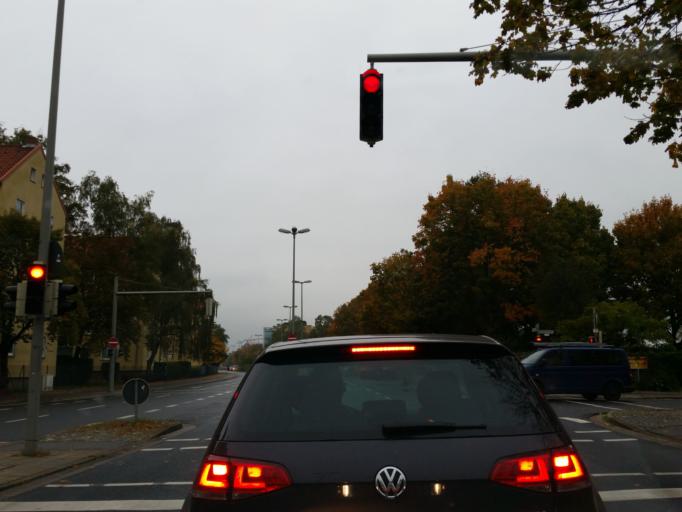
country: DE
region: Lower Saxony
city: Braunschweig
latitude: 52.2777
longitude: 10.5458
